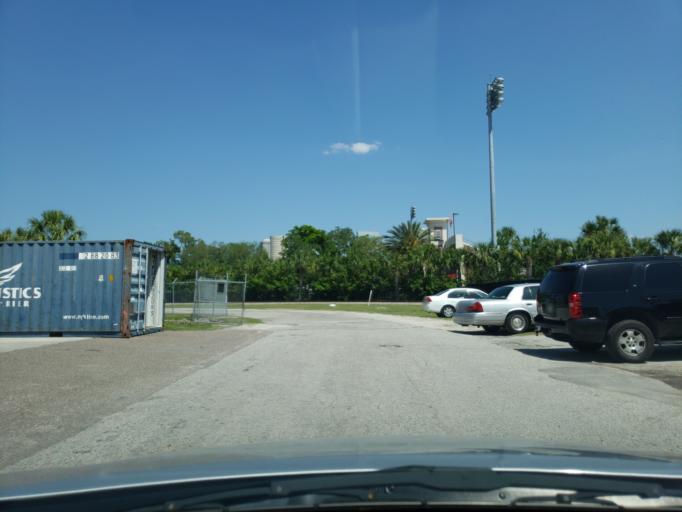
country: US
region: Florida
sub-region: Hillsborough County
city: Tampa
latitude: 27.9458
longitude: -82.4724
